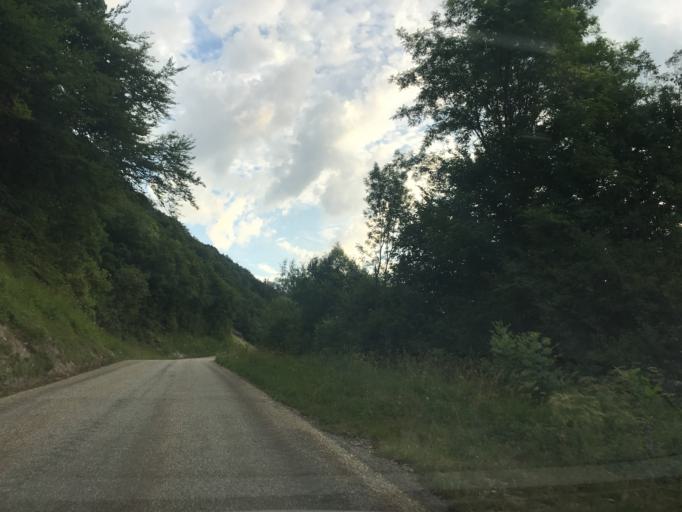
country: FR
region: Rhone-Alpes
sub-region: Departement de l'Isere
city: Saint-Vincent-de-Mercuze
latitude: 45.3945
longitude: 5.9554
